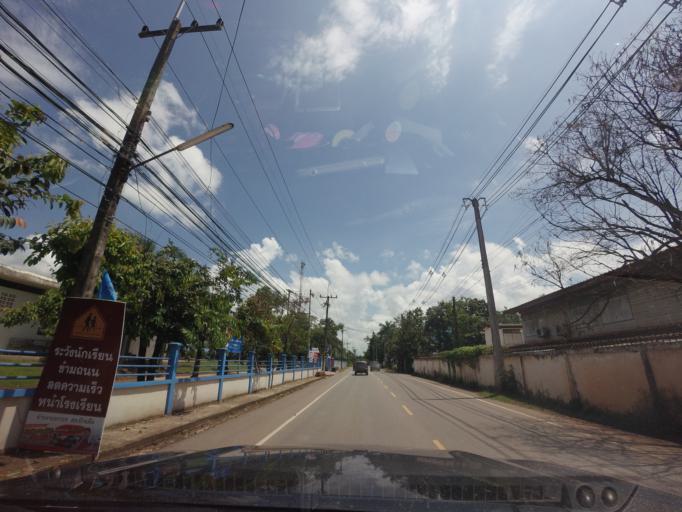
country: TH
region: Changwat Udon Thani
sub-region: Amphoe Ban Phue
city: Ban Phue
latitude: 17.6953
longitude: 102.4636
